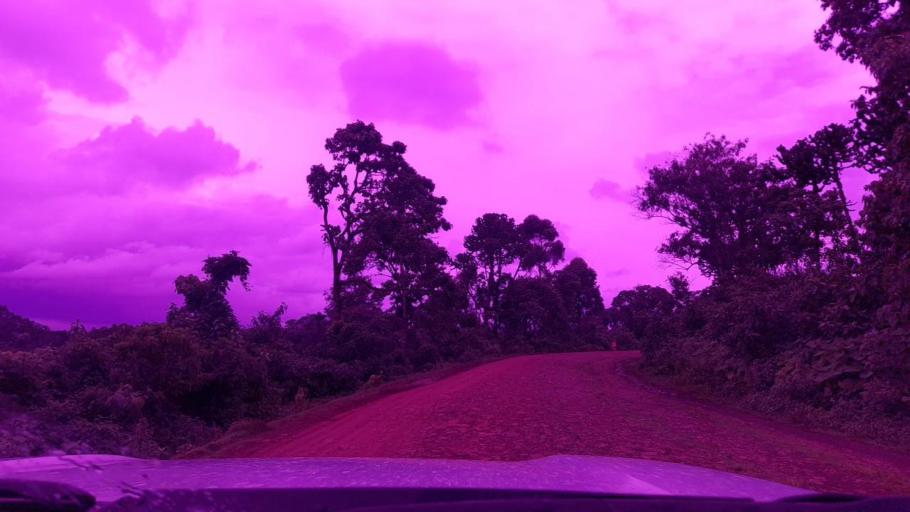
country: ET
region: Southern Nations, Nationalities, and People's Region
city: Tippi
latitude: 7.5733
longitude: 35.6403
